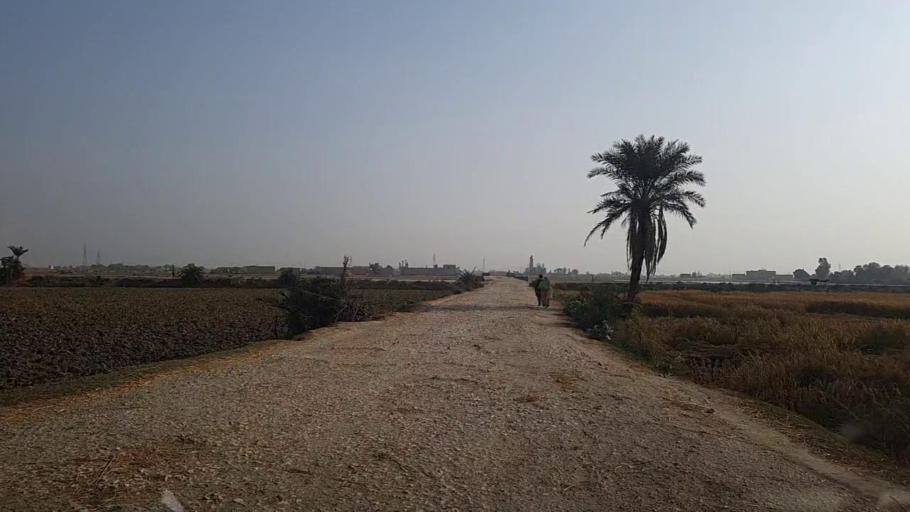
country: PK
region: Sindh
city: Kandhkot
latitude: 28.2815
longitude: 69.2563
